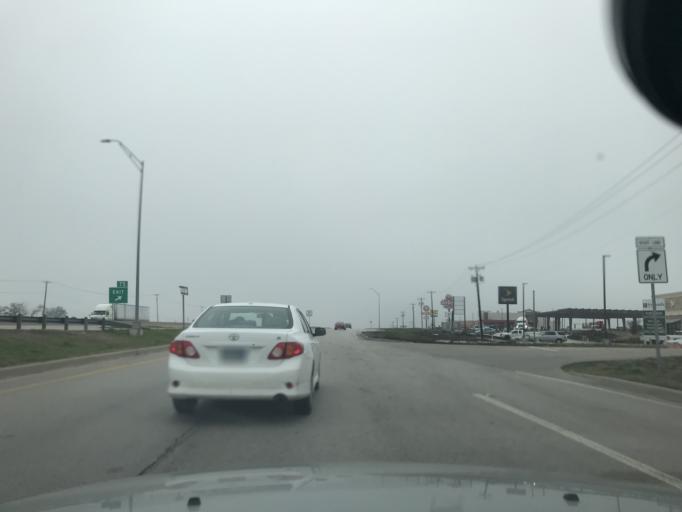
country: US
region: Texas
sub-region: Rockwall County
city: Royse City
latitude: 32.9630
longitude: -96.3433
